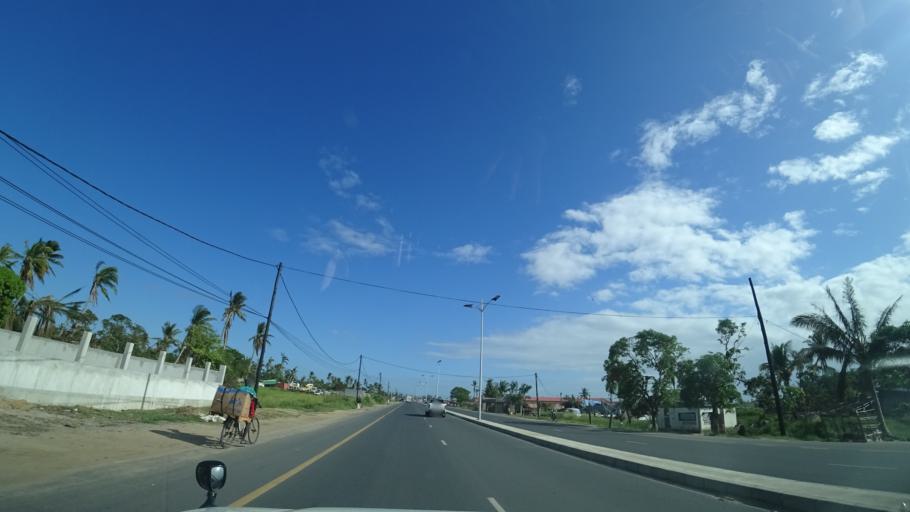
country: MZ
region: Sofala
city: Beira
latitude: -19.7478
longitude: 34.8718
